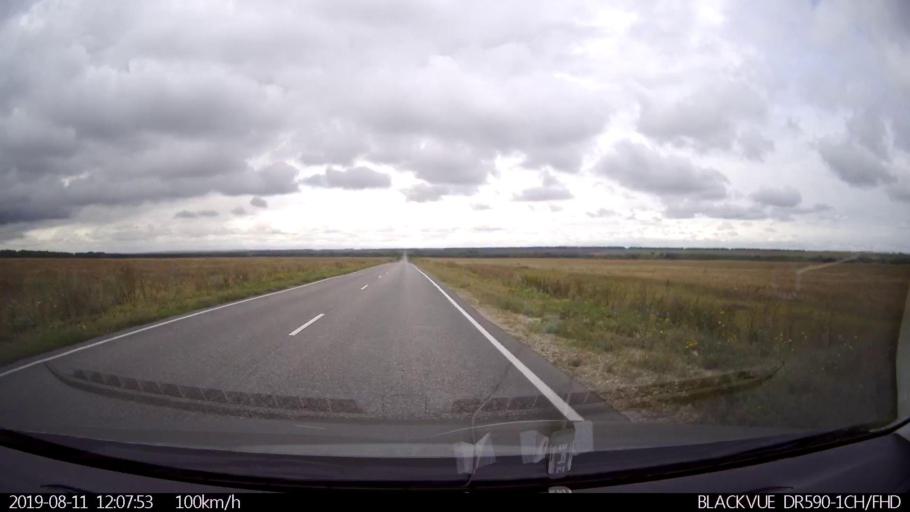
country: RU
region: Ulyanovsk
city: Silikatnyy
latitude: 53.9964
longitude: 48.0837
